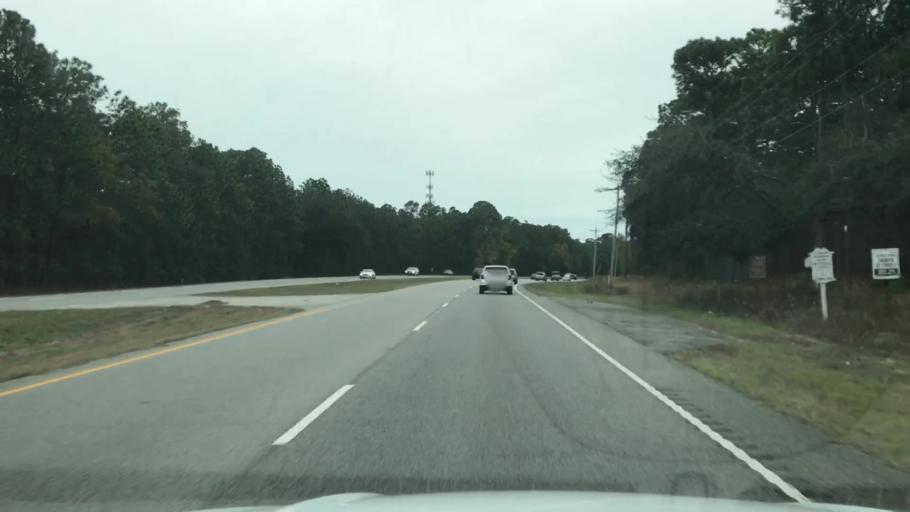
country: US
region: South Carolina
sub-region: Georgetown County
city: Georgetown
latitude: 33.3679
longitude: -79.2209
